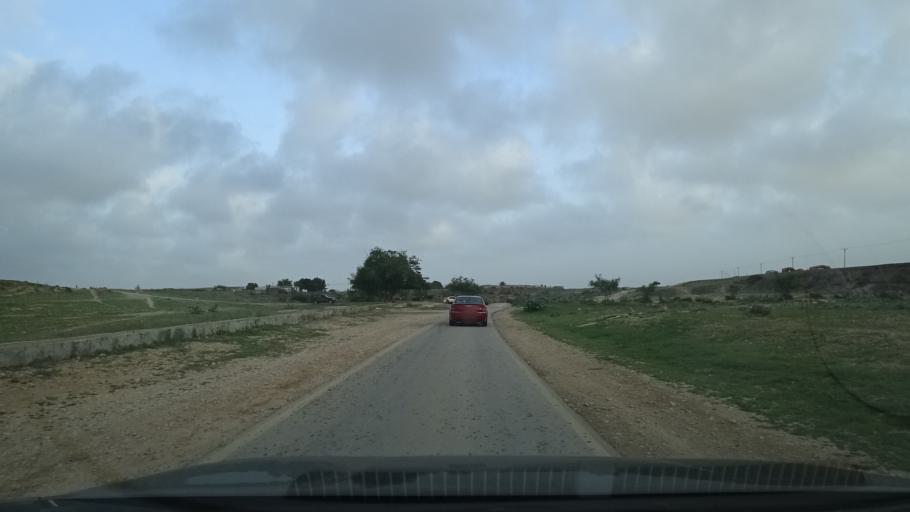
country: OM
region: Zufar
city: Salalah
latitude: 17.1024
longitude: 54.2327
